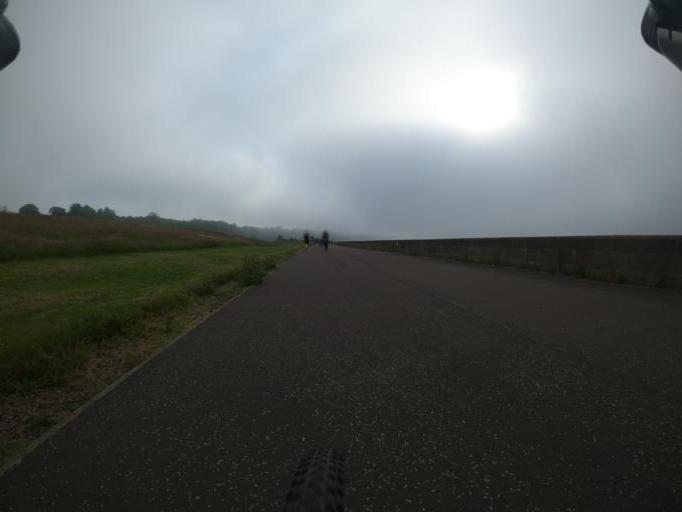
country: GB
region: Scotland
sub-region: Edinburgh
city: Edinburgh
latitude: 55.9820
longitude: -3.2555
